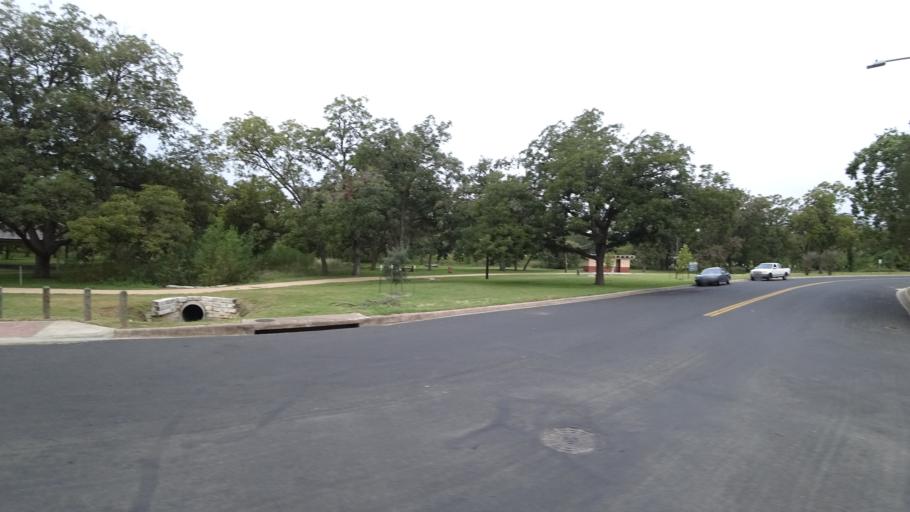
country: US
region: Texas
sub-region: Travis County
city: Austin
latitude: 30.2676
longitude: -97.7136
